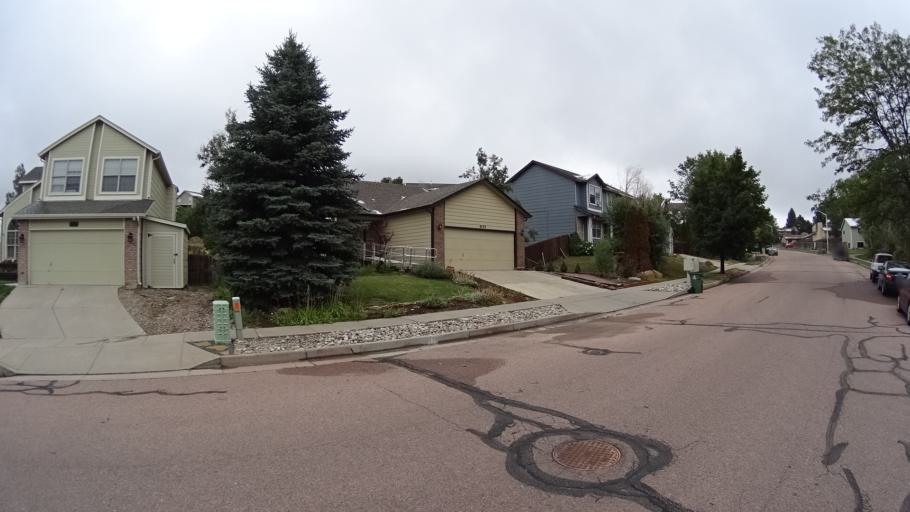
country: US
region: Colorado
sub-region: El Paso County
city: Cimarron Hills
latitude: 38.9196
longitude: -104.7601
